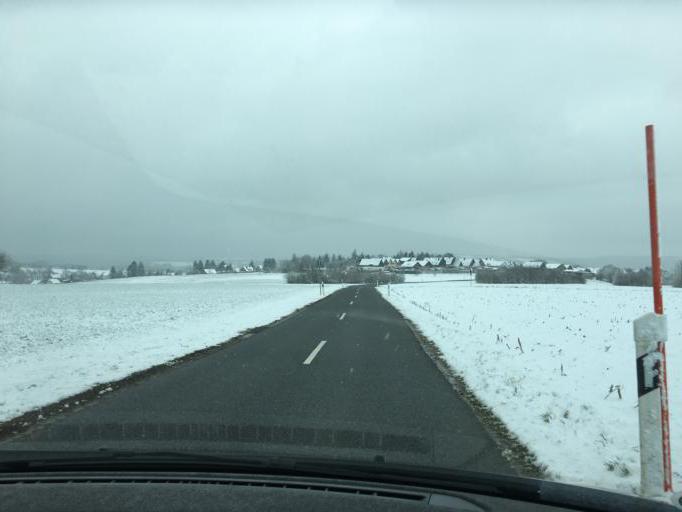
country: DE
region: North Rhine-Westphalia
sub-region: Regierungsbezirk Koln
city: Hurtgenwald
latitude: 50.7064
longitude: 6.4116
